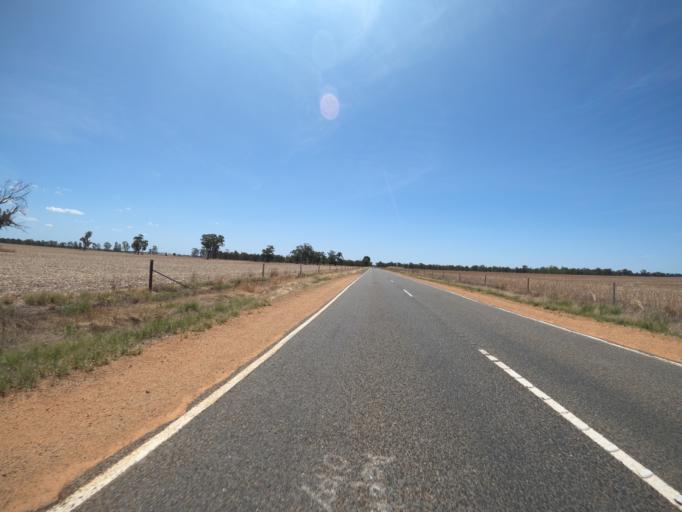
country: AU
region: Victoria
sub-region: Moira
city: Yarrawonga
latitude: -36.1675
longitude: 145.9672
